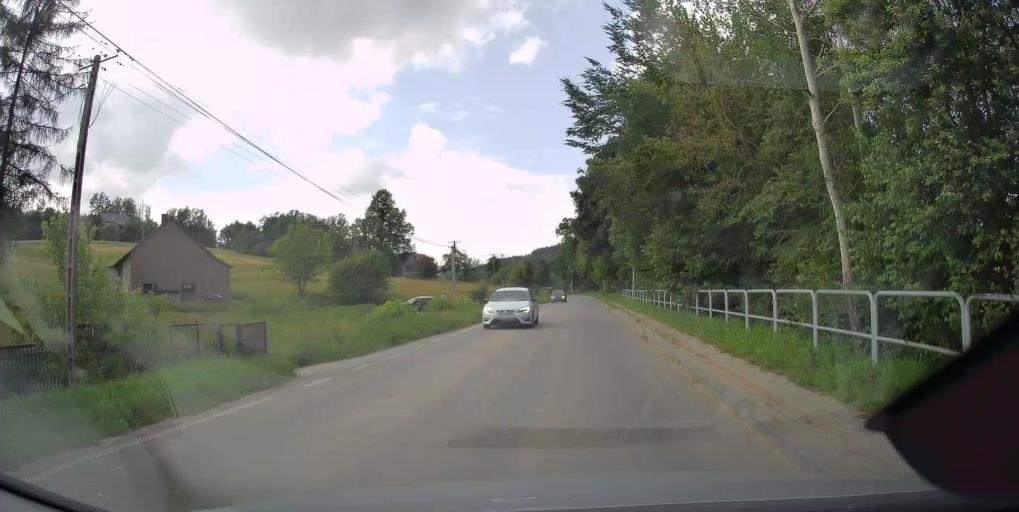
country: PL
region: Lesser Poland Voivodeship
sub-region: Powiat nowosadecki
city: Korzenna
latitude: 49.7540
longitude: 20.7759
